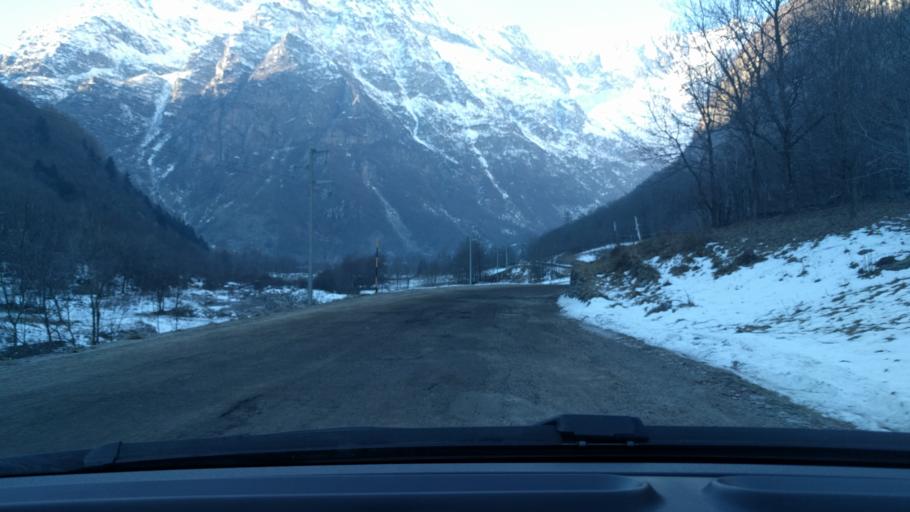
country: IT
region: Piedmont
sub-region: Provincia di Torino
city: Groscavallo
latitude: 45.3657
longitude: 7.2380
